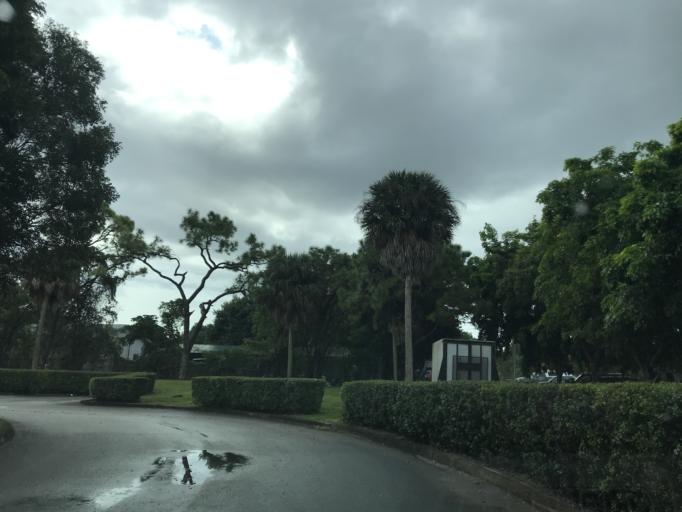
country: US
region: Florida
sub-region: Palm Beach County
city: Delray Beach
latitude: 26.4517
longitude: -80.0962
